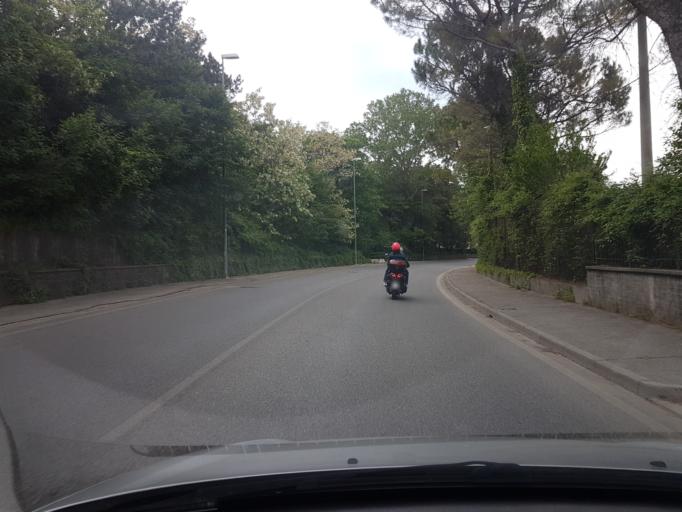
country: IT
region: Friuli Venezia Giulia
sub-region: Provincia di Trieste
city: Muggia
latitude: 45.5993
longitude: 13.7792
